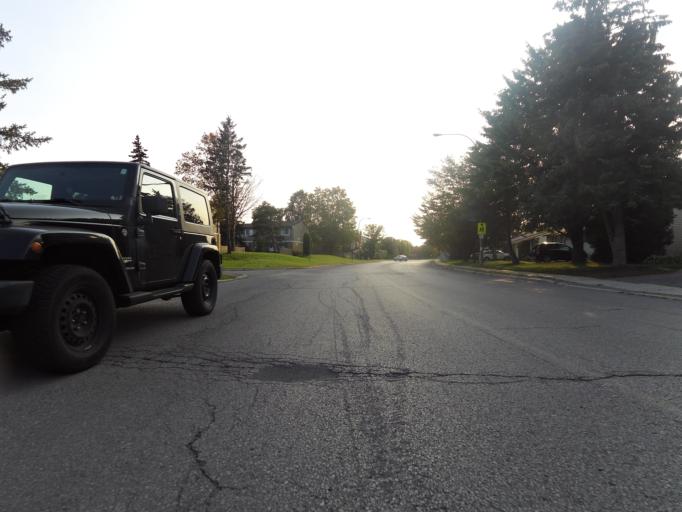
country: CA
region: Ontario
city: Bells Corners
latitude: 45.2809
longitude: -75.7574
